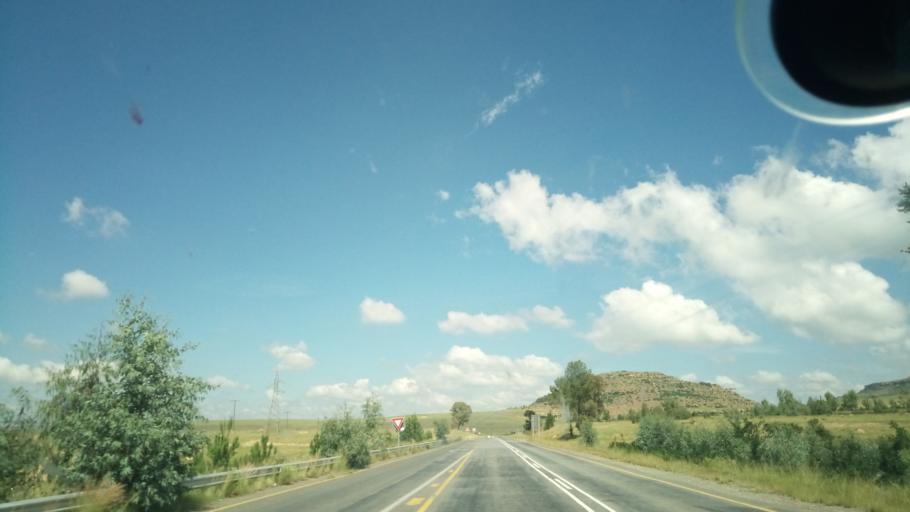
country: ZA
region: Orange Free State
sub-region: Thabo Mofutsanyana District Municipality
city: Ficksburg
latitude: -28.8905
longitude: 27.8569
